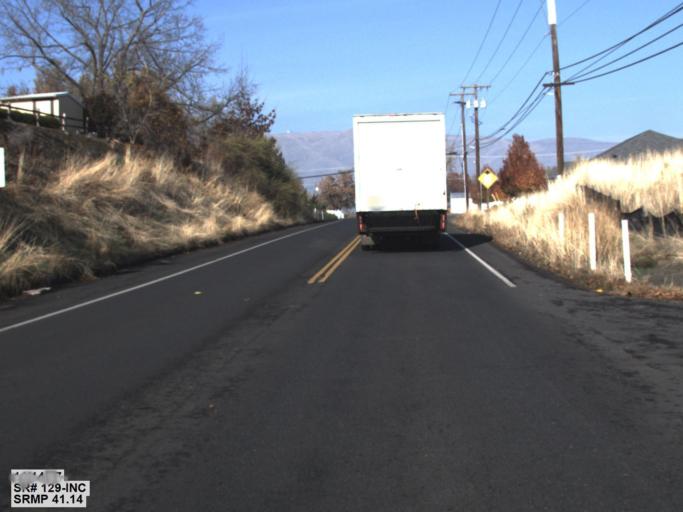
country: US
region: Washington
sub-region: Asotin County
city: Clarkston
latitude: 46.4016
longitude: -117.0443
